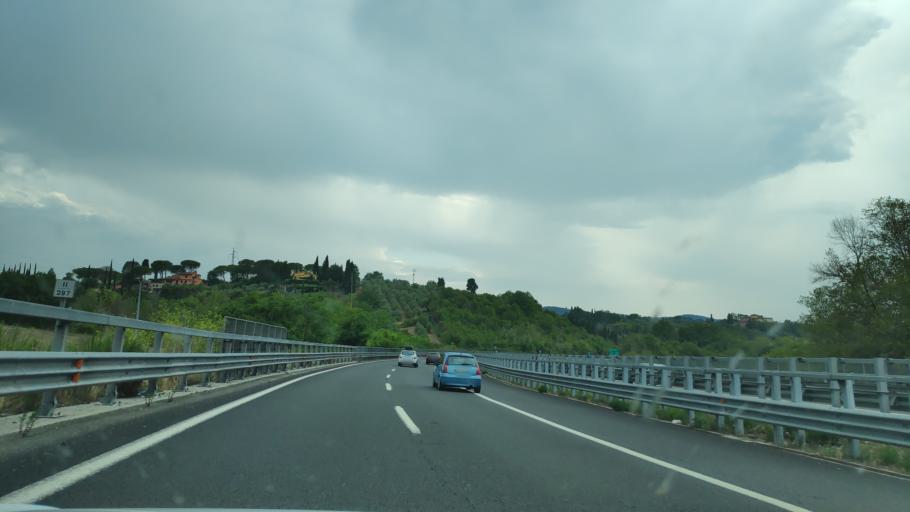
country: IT
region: Tuscany
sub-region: Province of Florence
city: Tavarnuzze
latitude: 43.7213
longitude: 11.2416
